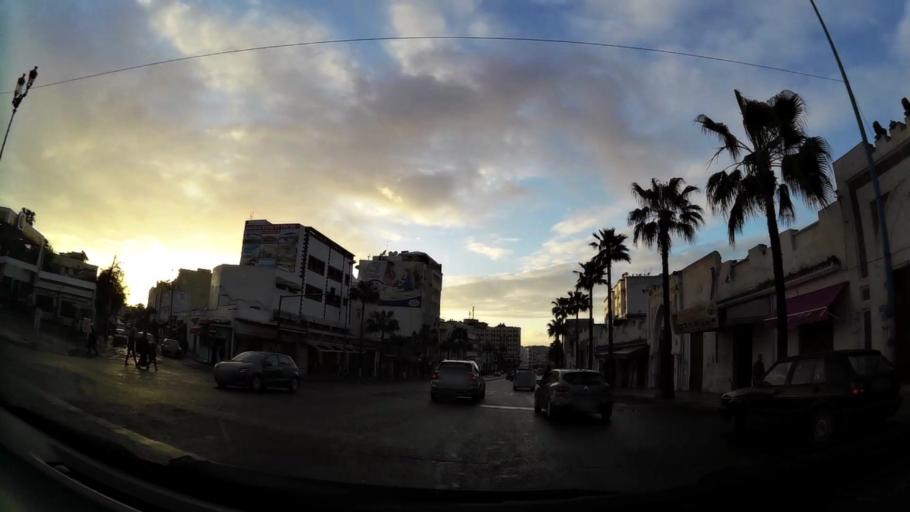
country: MA
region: Grand Casablanca
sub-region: Casablanca
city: Casablanca
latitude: 33.5838
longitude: -7.6047
